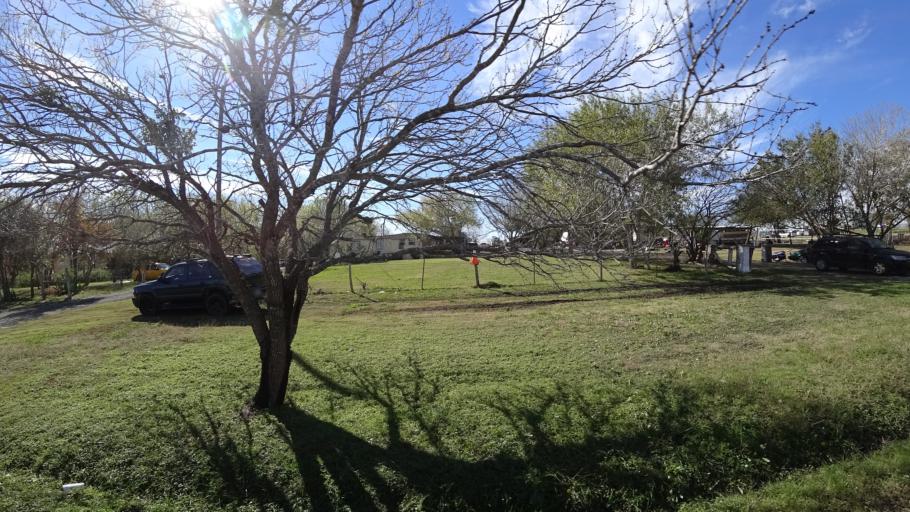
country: US
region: Texas
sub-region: Travis County
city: Onion Creek
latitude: 30.1192
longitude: -97.6897
